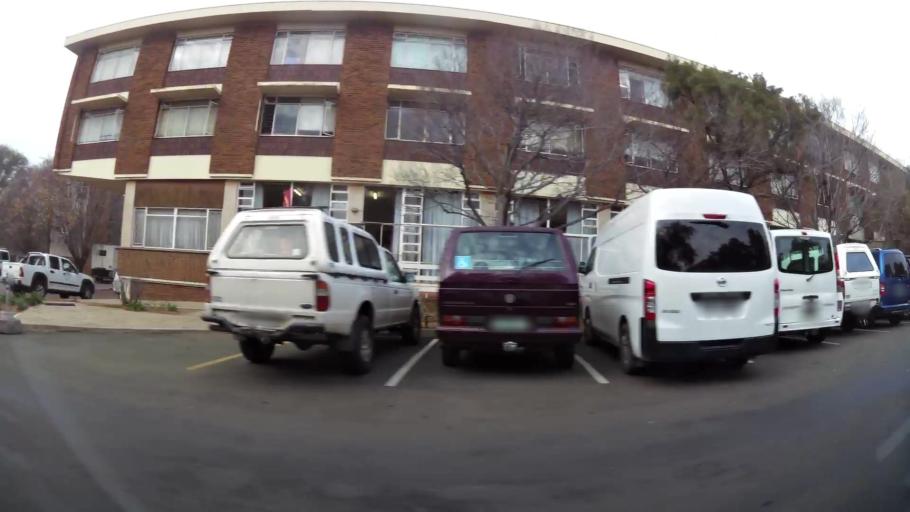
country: ZA
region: Orange Free State
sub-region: Mangaung Metropolitan Municipality
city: Bloemfontein
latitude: -29.1102
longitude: 26.1892
